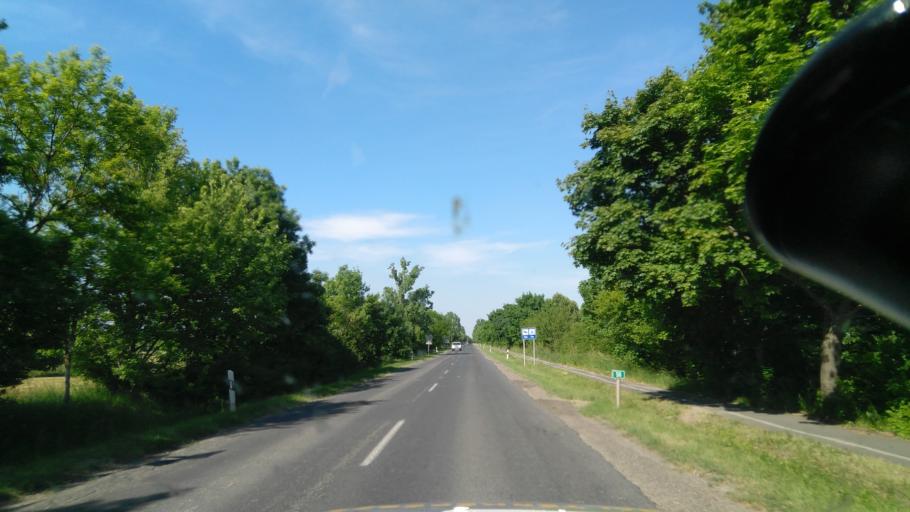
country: HU
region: Bekes
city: Sarkad
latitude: 46.7190
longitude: 21.3337
